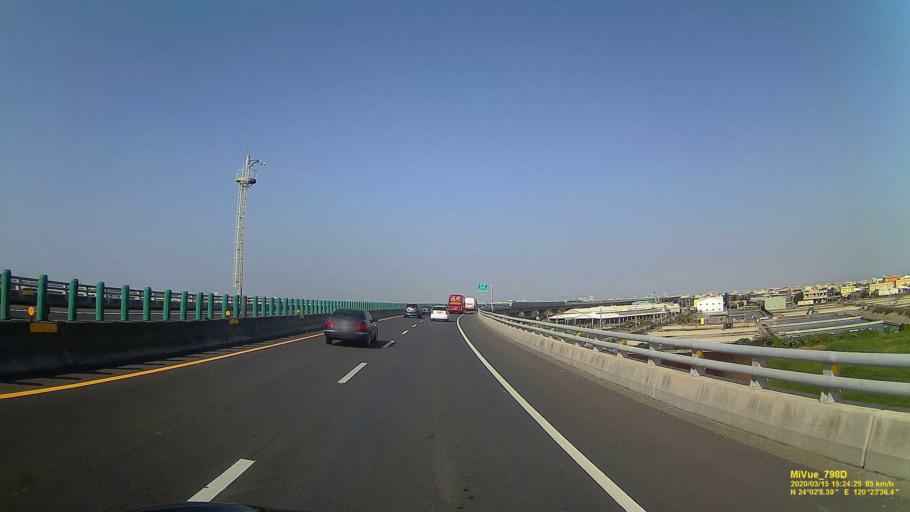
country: TW
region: Taiwan
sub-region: Changhua
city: Chang-hua
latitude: 24.0362
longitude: 120.3941
